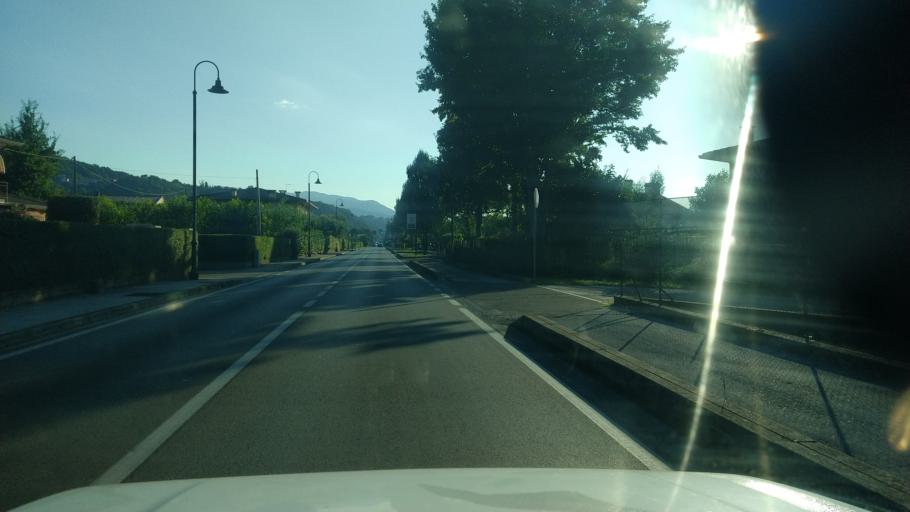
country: IT
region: Veneto
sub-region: Provincia di Vicenza
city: Pianezze
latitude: 45.7325
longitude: 11.6322
